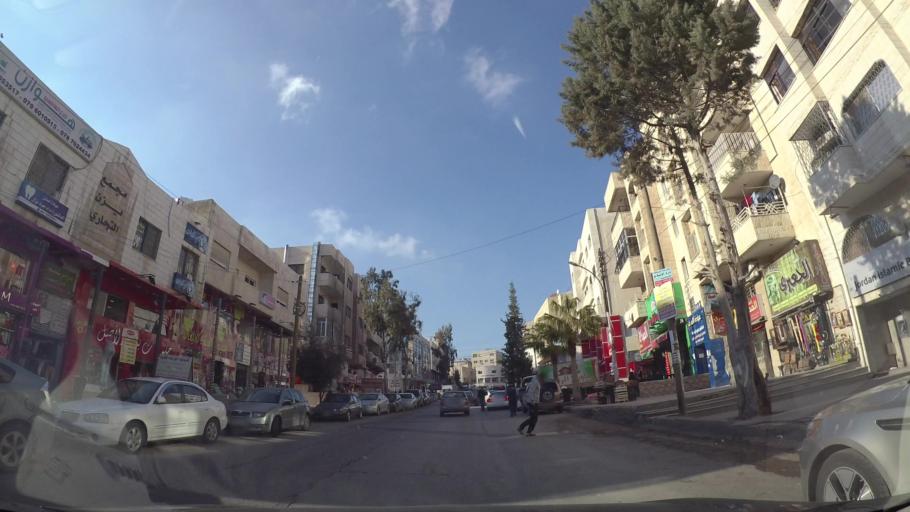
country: JO
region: Amman
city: Amman
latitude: 31.9746
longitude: 35.9500
